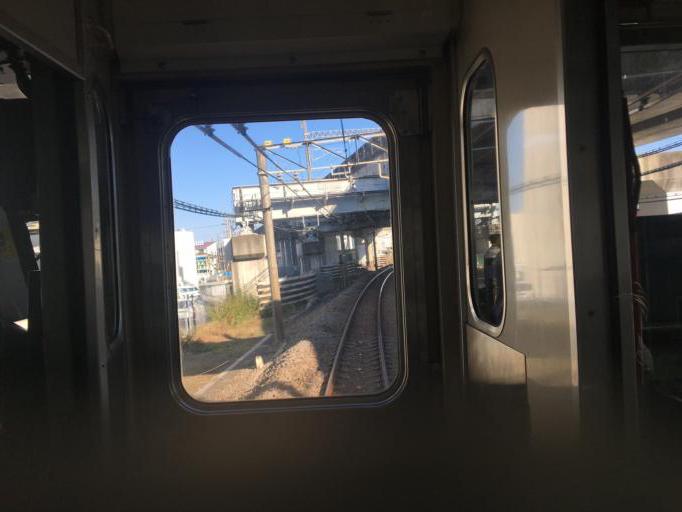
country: JP
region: Gunma
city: Takasaki
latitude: 36.3346
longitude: 139.0113
